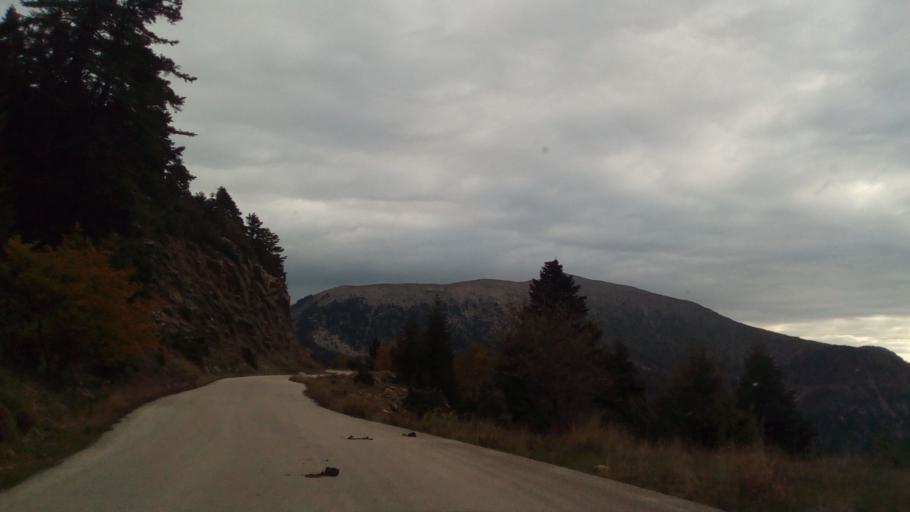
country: GR
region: West Greece
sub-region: Nomos Aitolias kai Akarnanias
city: Thermo
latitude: 38.6213
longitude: 21.8195
